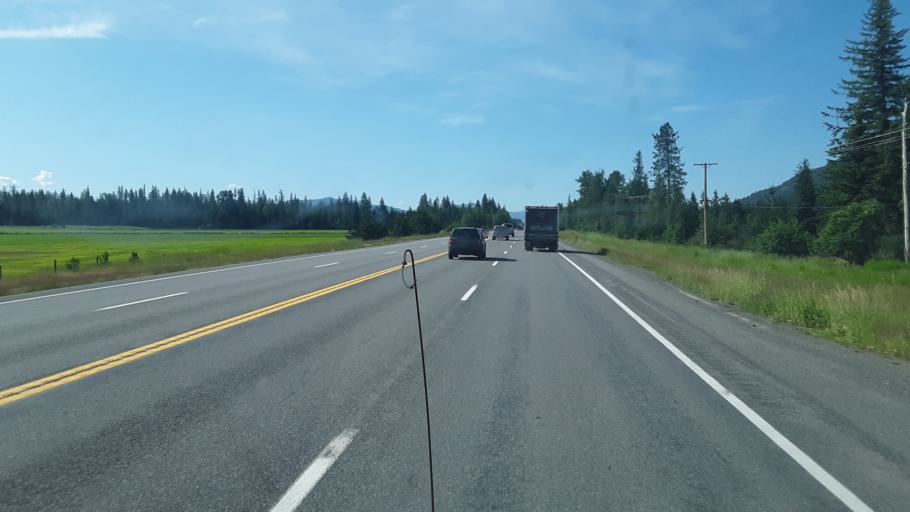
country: US
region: Idaho
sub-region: Bonner County
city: Ponderay
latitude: 48.3705
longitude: -116.5472
